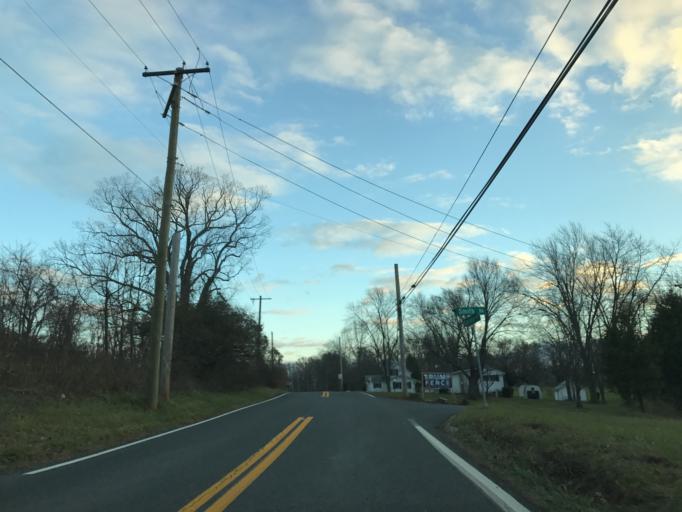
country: US
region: Maryland
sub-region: Cecil County
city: Rising Sun
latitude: 39.6678
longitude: -76.2114
